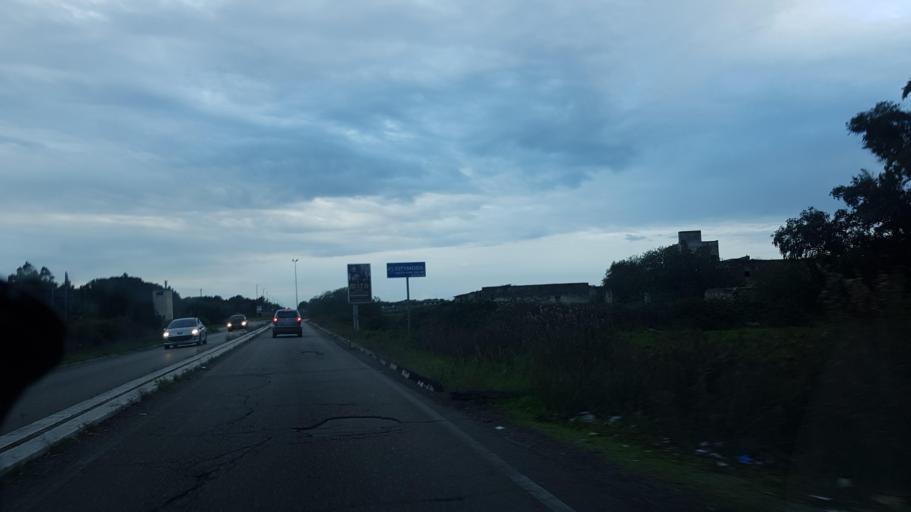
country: IT
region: Apulia
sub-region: Provincia di Lecce
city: Merine
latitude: 40.3443
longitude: 18.2047
